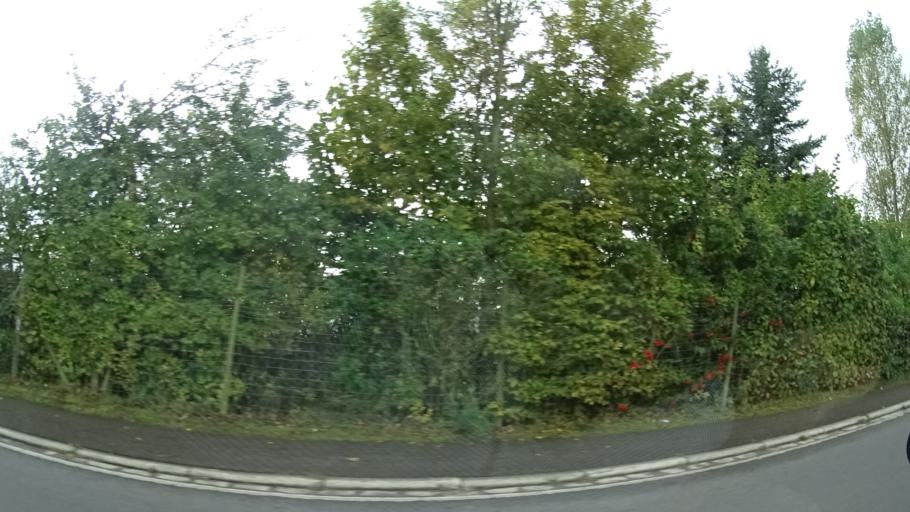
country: DE
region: Baden-Wuerttemberg
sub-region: Karlsruhe Region
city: Malsch
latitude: 49.2441
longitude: 8.6881
